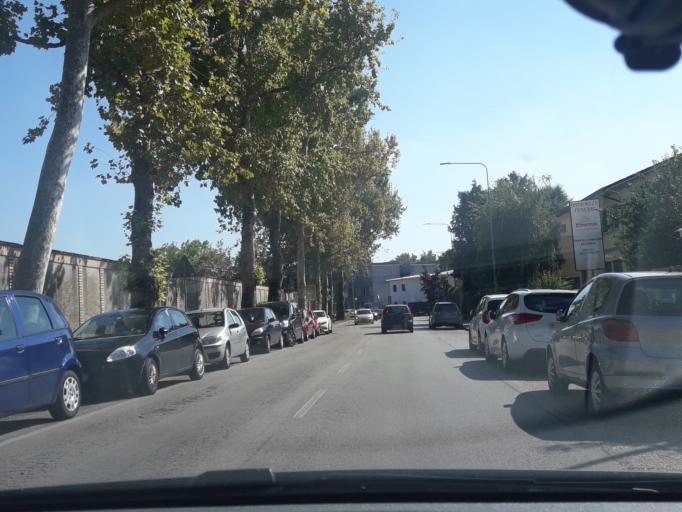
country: IT
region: Friuli Venezia Giulia
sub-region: Provincia di Udine
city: Udine
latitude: 46.0769
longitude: 13.2243
